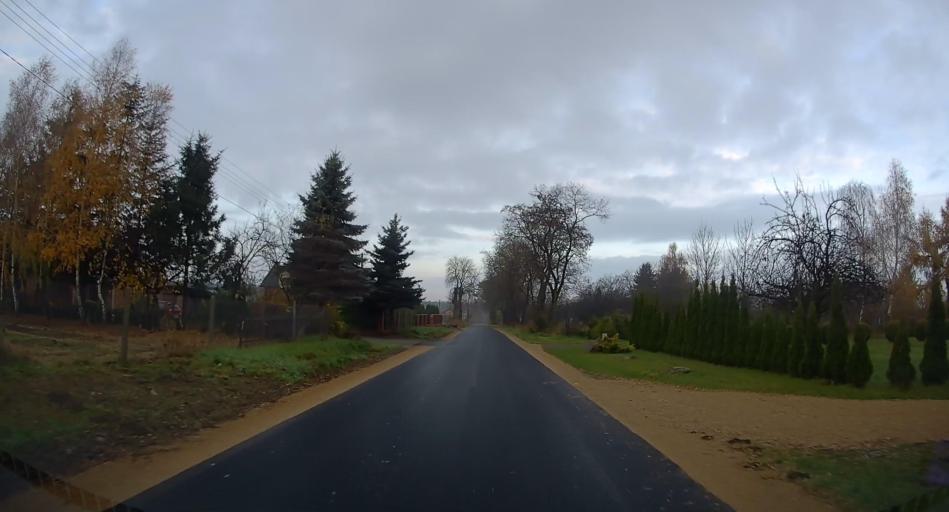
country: PL
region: Lodz Voivodeship
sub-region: Powiat skierniewicki
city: Kowiesy
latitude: 51.9260
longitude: 20.4057
